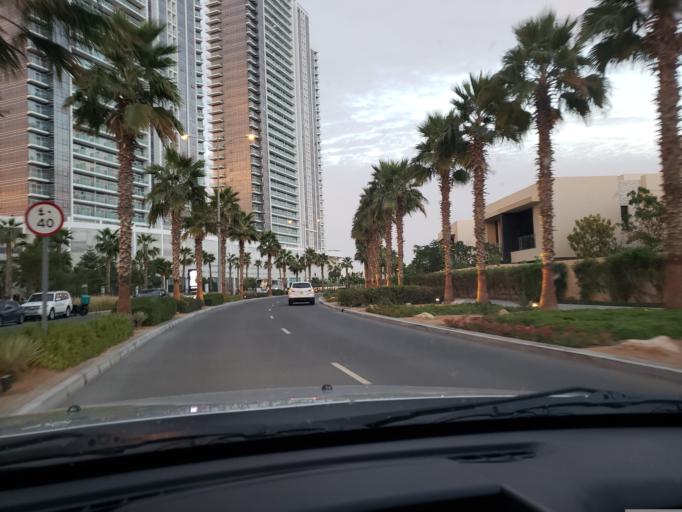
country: AE
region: Dubai
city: Dubai
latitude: 25.0236
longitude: 55.2433
